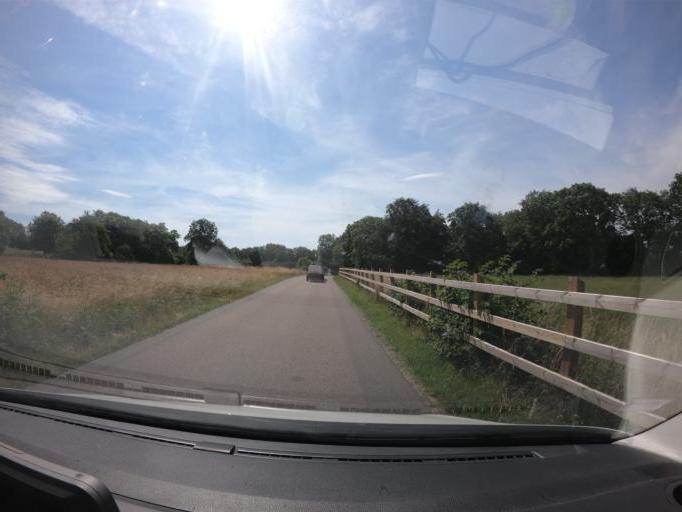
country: SE
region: Skane
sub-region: Angelholms Kommun
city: Vejbystrand
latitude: 56.4530
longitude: 12.7042
